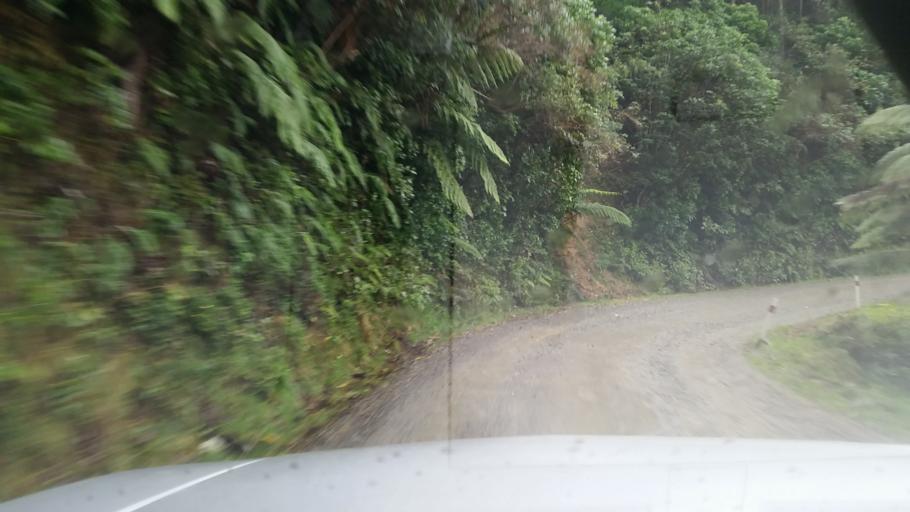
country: NZ
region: Marlborough
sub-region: Marlborough District
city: Picton
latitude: -41.1390
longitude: 174.0517
